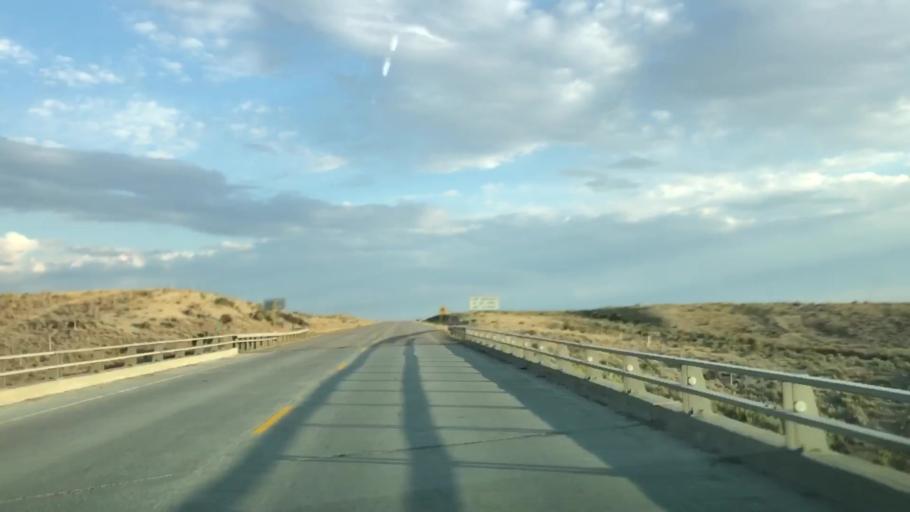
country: US
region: Wyoming
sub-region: Sweetwater County
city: North Rock Springs
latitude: 42.0998
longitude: -109.4456
